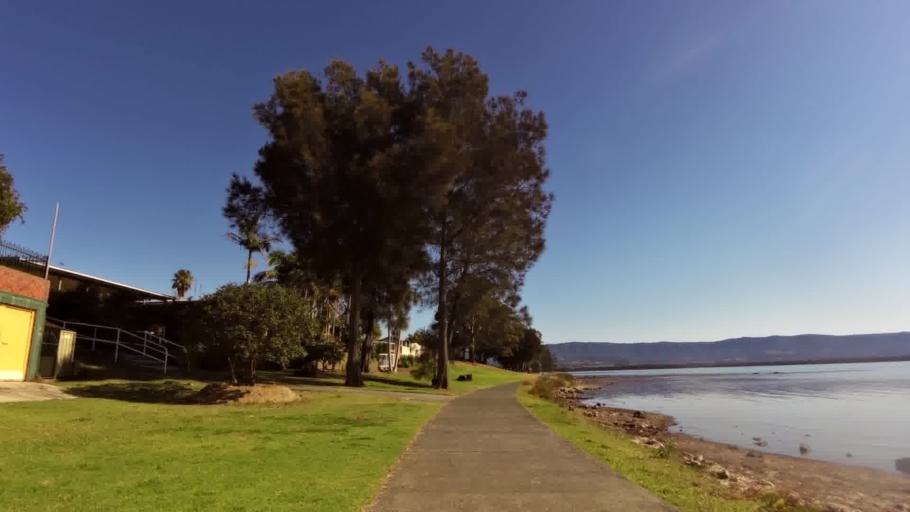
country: AU
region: New South Wales
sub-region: Shellharbour
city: Barrack Heights
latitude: -34.5569
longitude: 150.8310
